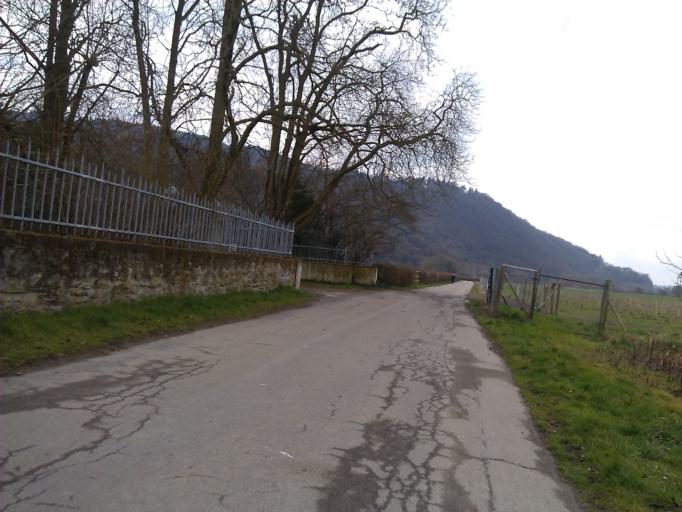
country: DE
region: Rheinland-Pfalz
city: Leutesdorf
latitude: 50.4566
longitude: 7.3577
